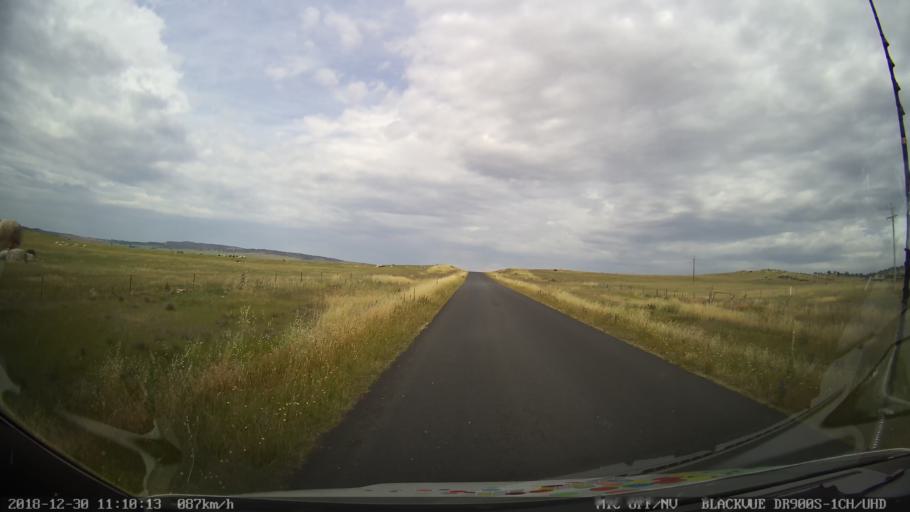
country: AU
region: New South Wales
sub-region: Snowy River
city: Berridale
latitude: -36.5128
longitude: 148.7839
